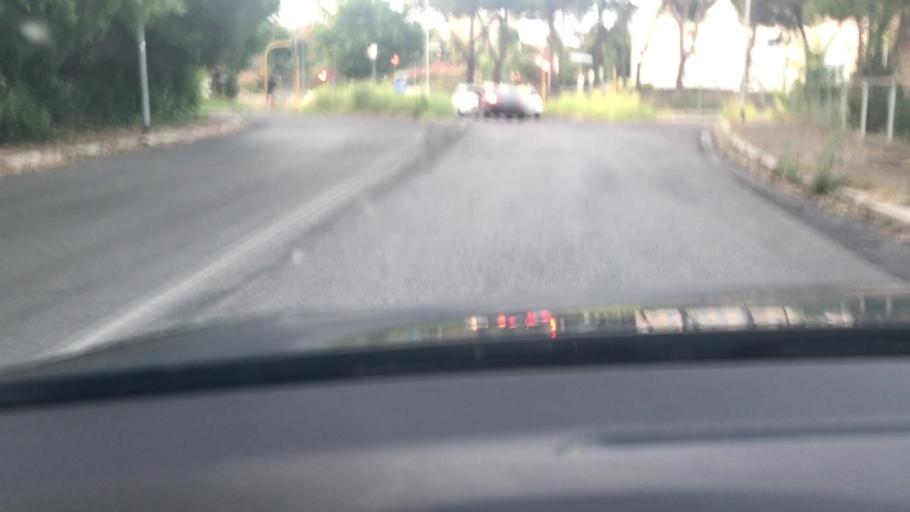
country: IT
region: Latium
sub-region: Citta metropolitana di Roma Capitale
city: Rome
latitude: 41.9275
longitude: 12.5640
